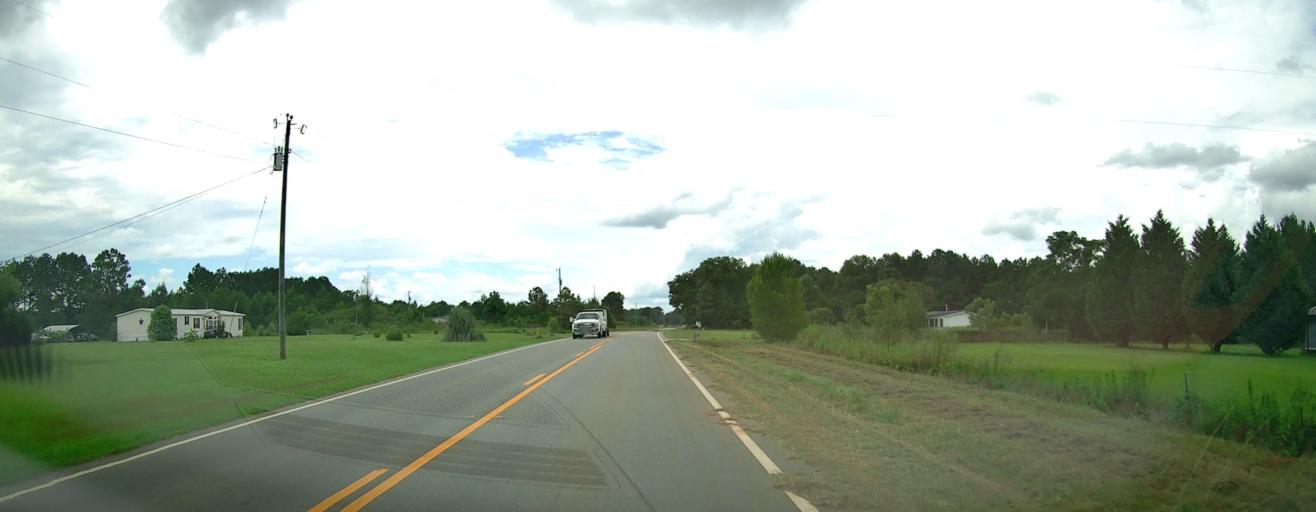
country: US
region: Georgia
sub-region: Macon County
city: Oglethorpe
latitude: 32.2692
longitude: -84.1139
